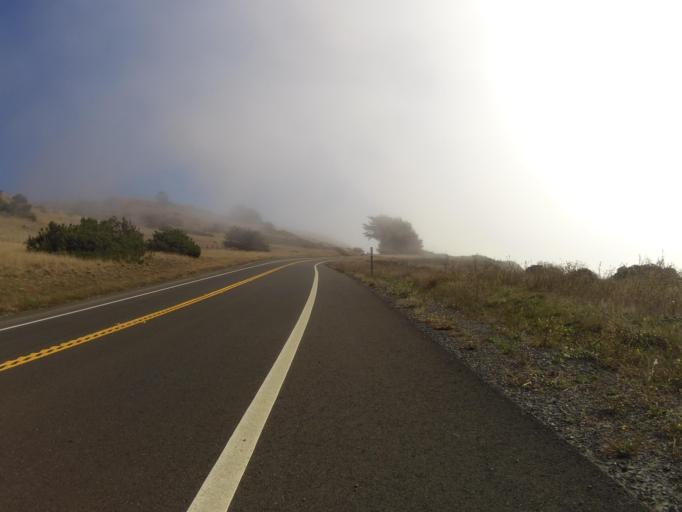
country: US
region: California
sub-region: Sonoma County
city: Sea Ranch
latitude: 38.8639
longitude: -123.6549
